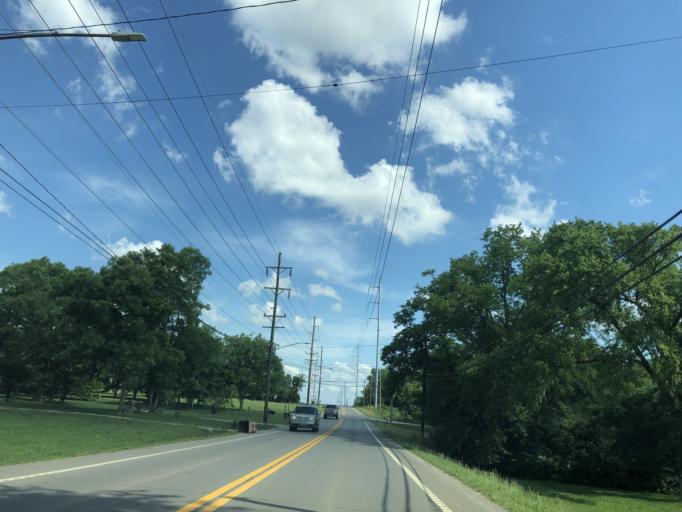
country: US
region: Tennessee
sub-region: Davidson County
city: Nashville
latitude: 36.2387
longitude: -86.8187
